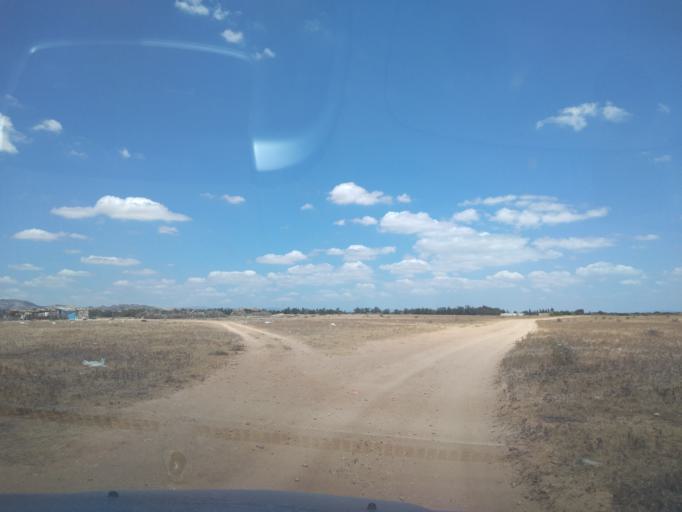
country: TN
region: Susah
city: Harqalah
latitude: 36.1703
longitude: 10.4353
